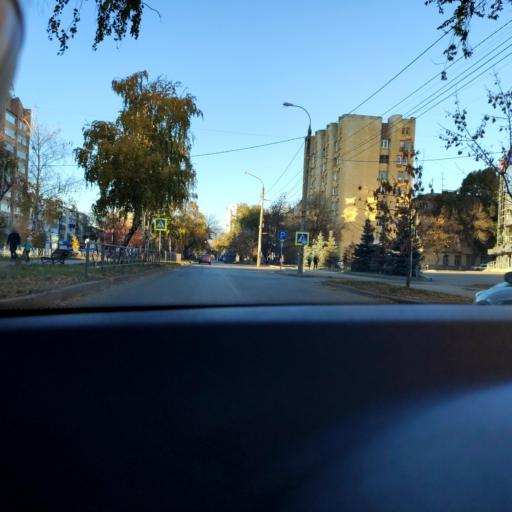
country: RU
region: Samara
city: Samara
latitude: 53.1935
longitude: 50.1790
